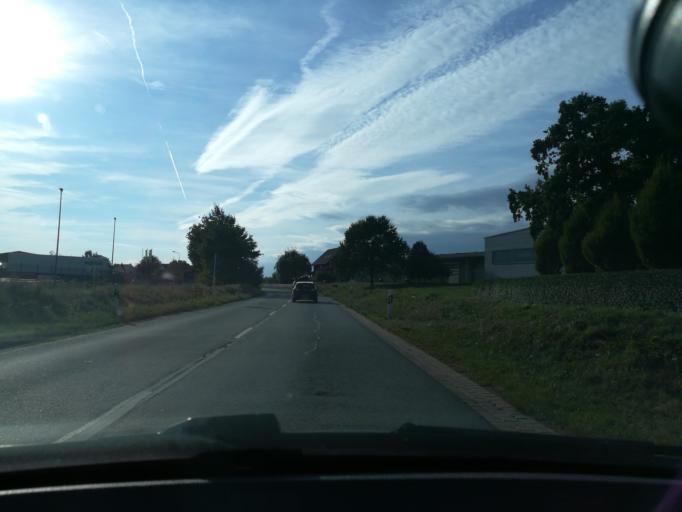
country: DE
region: North Rhine-Westphalia
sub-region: Regierungsbezirk Detmold
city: Minden
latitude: 52.3070
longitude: 8.9499
